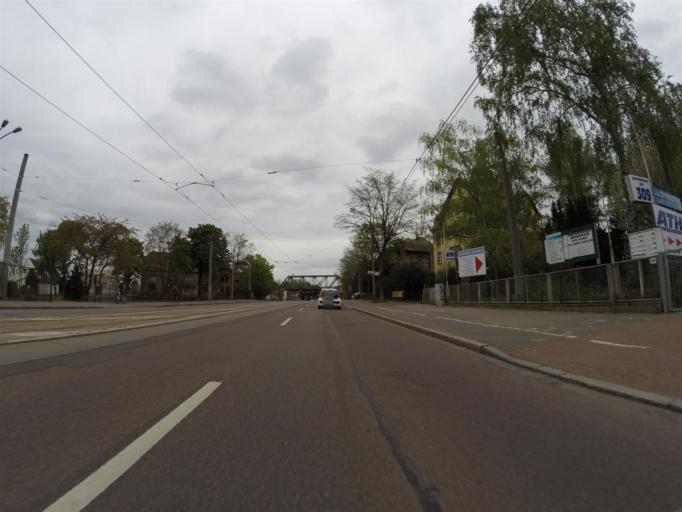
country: DE
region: Saxony-Anhalt
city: Schkopau
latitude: 51.4458
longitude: 11.9840
